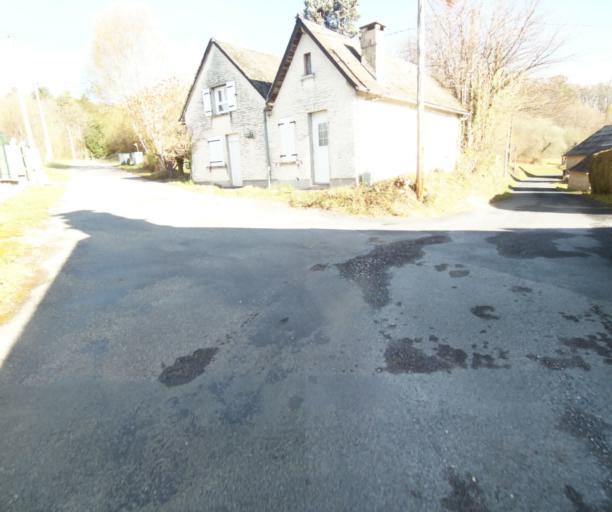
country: FR
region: Limousin
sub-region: Departement de la Correze
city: Laguenne
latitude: 45.2749
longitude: 1.8644
